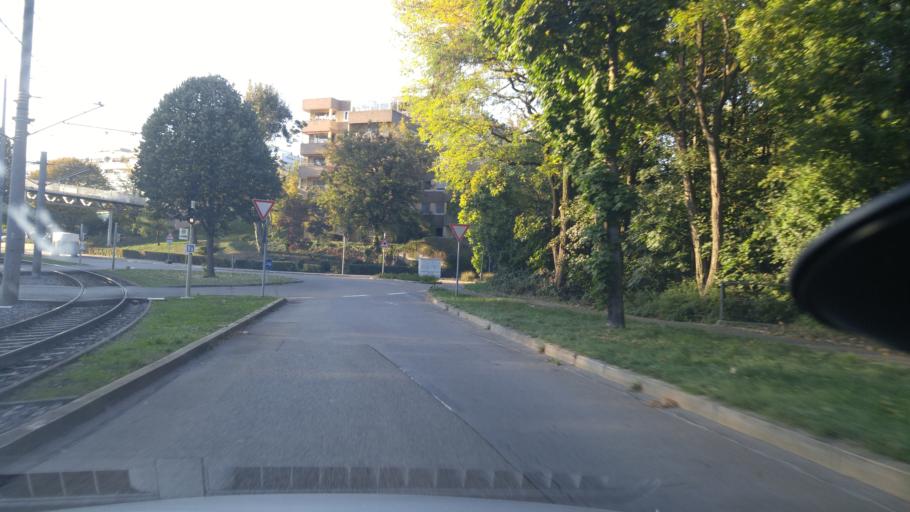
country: DE
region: Baden-Wuerttemberg
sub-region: Regierungsbezirk Stuttgart
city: Stuttgart Feuerbach
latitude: 48.7793
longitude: 9.1339
